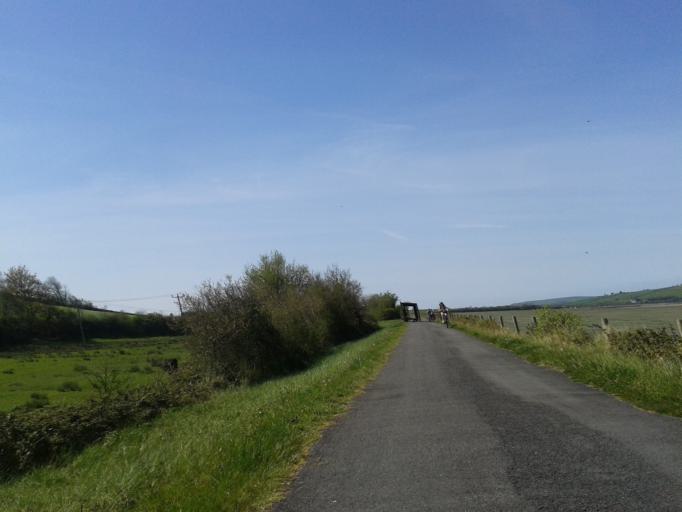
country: GB
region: England
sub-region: Devon
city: Barnstaple
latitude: 51.0788
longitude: -4.0872
